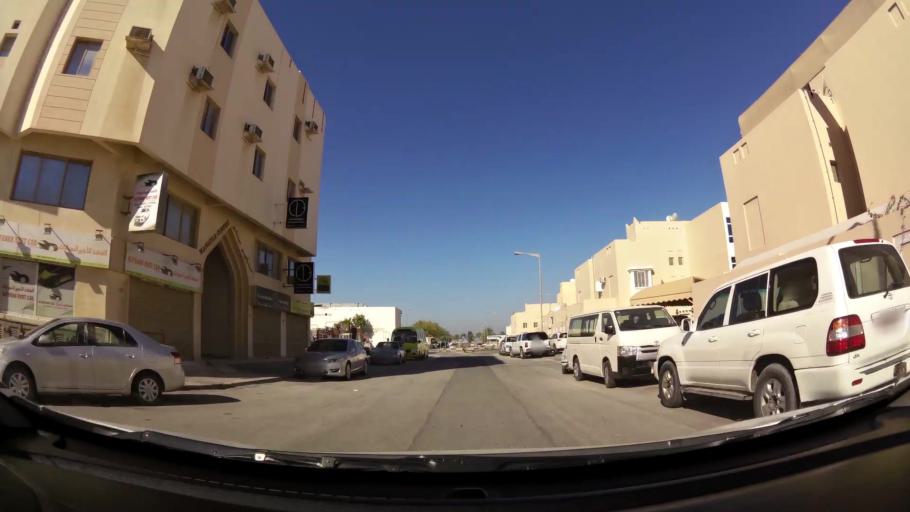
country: BH
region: Muharraq
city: Al Muharraq
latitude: 26.2565
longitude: 50.6065
